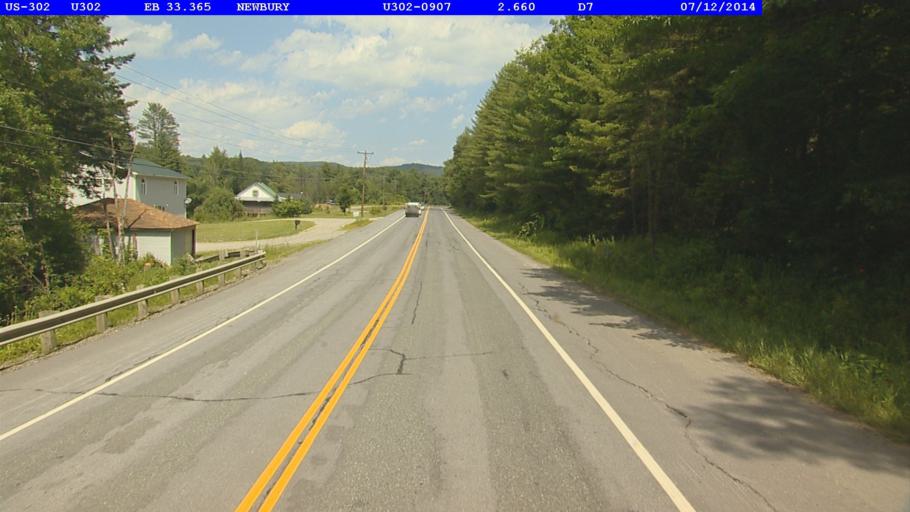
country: US
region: New Hampshire
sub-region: Grafton County
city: Woodsville
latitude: 44.1520
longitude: -72.0816
